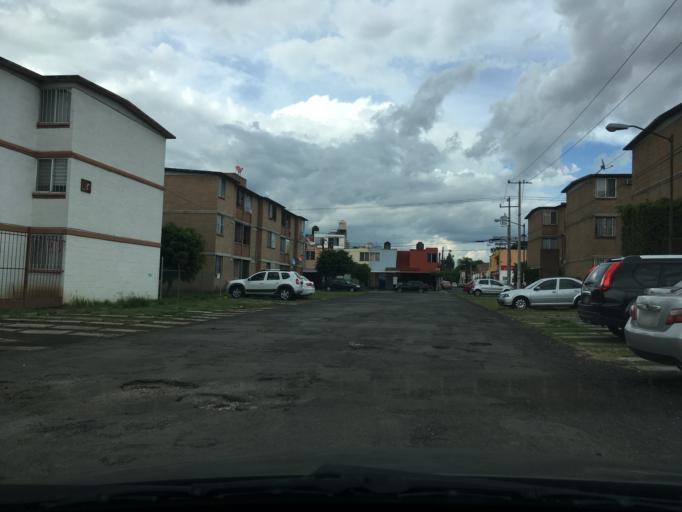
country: MX
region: Michoacan
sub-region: Morelia
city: Morelos
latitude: 19.6718
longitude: -101.2254
